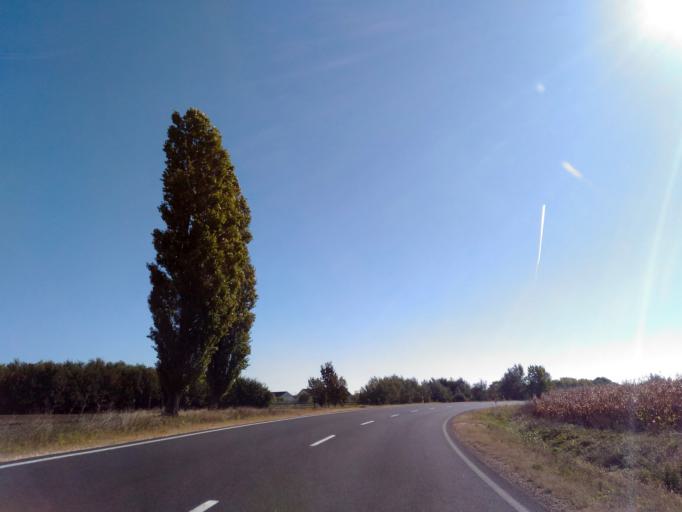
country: HU
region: Fejer
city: Ivancsa
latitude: 47.1330
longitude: 18.8133
